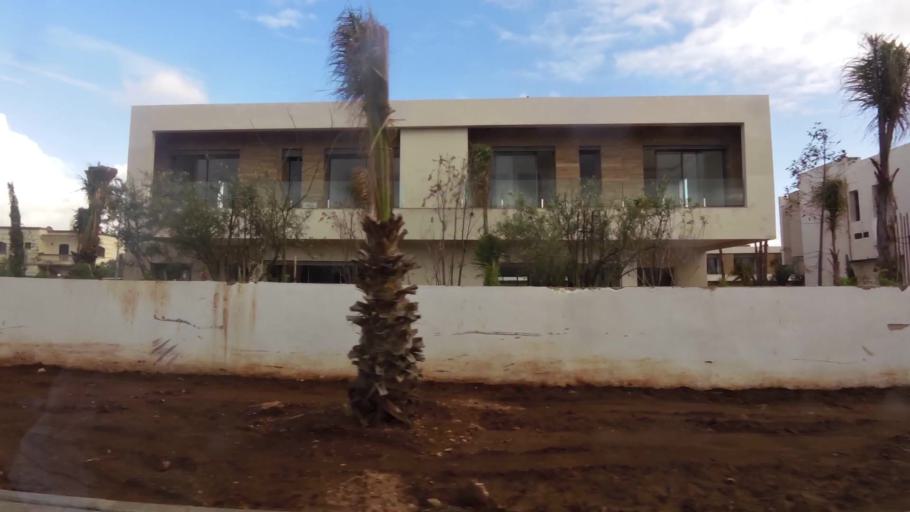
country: MA
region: Grand Casablanca
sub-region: Casablanca
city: Casablanca
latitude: 33.5778
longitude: -7.6965
